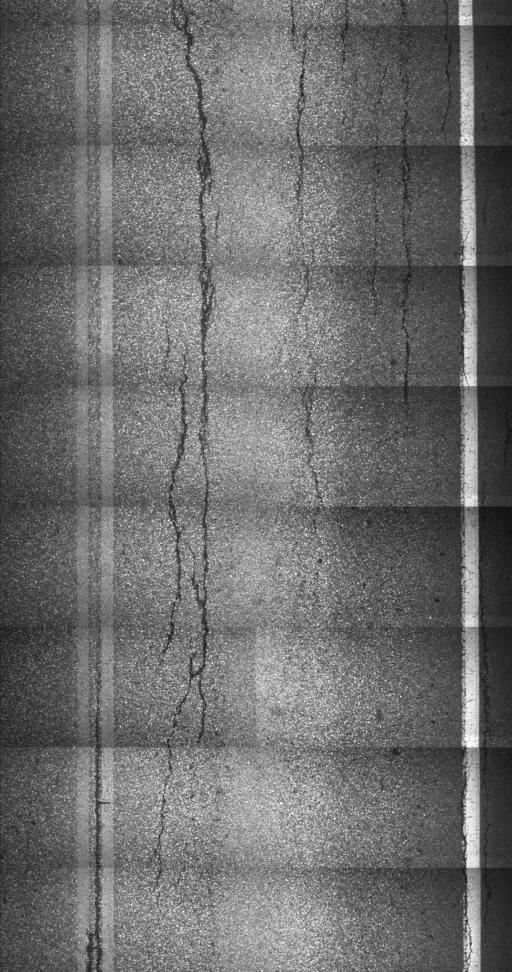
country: US
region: Vermont
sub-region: Rutland County
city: West Rutland
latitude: 43.4899
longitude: -73.0761
